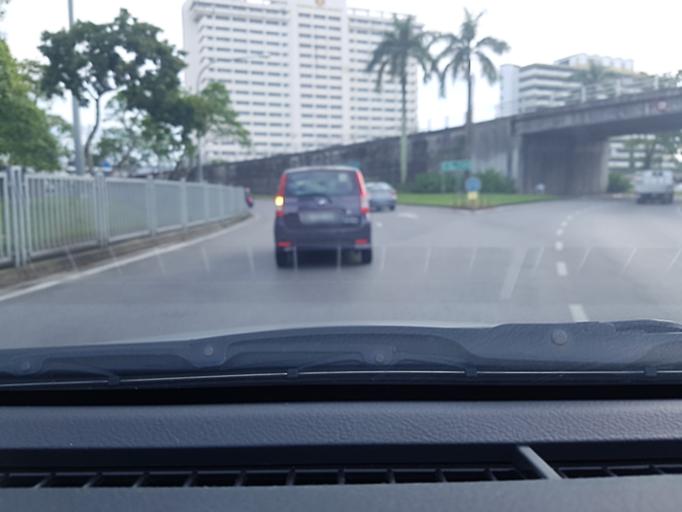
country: MY
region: Sarawak
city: Kuching
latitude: 1.5312
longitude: 110.3586
